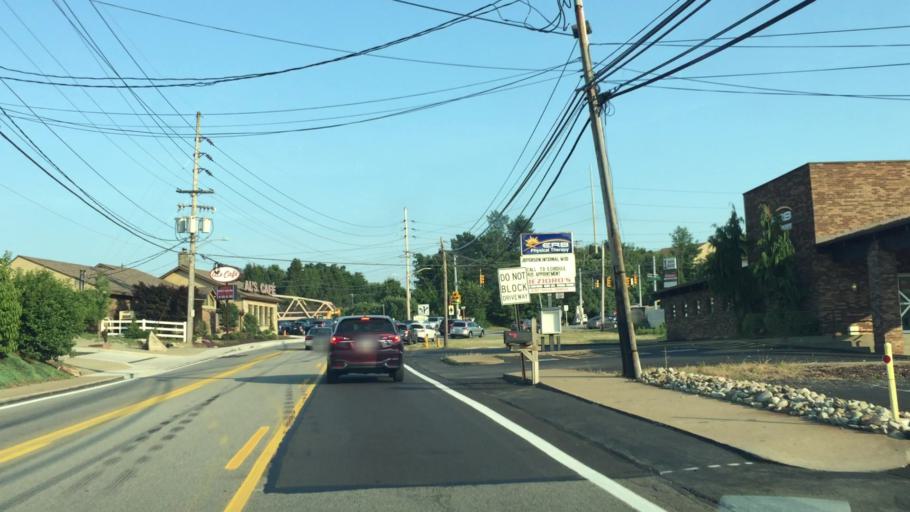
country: US
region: Pennsylvania
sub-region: Allegheny County
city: Bryn Mawr
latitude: 40.3130
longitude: -80.0665
